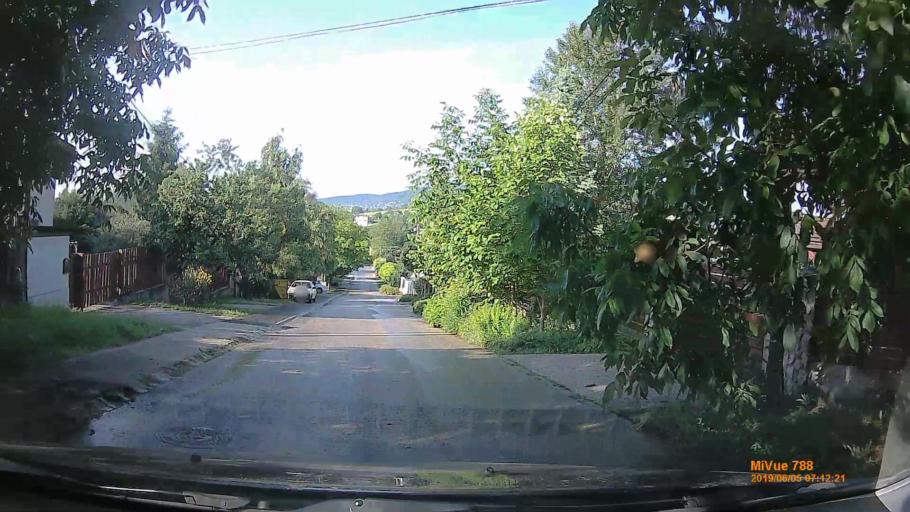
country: HU
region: Pest
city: Urom
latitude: 47.5826
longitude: 19.0311
